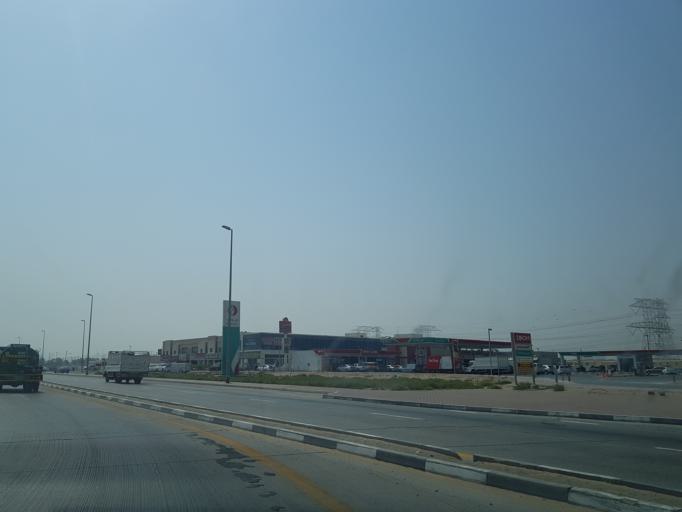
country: AE
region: Ash Shariqah
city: Sharjah
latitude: 25.1649
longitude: 55.3809
